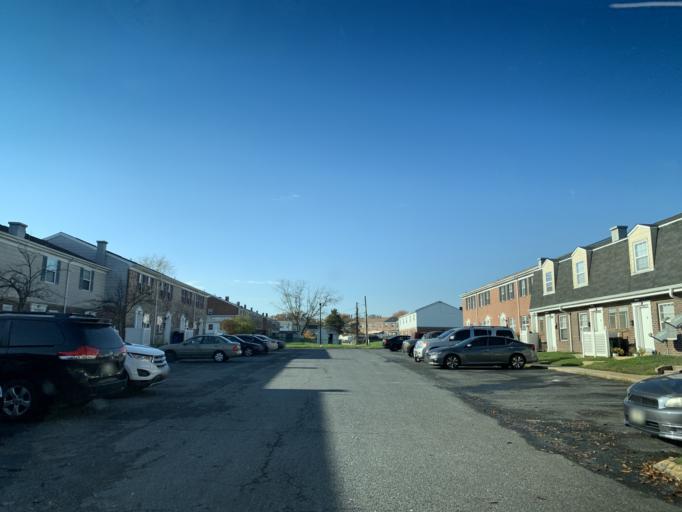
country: US
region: Maryland
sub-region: Baltimore County
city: Middle River
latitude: 39.3483
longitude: -76.4435
